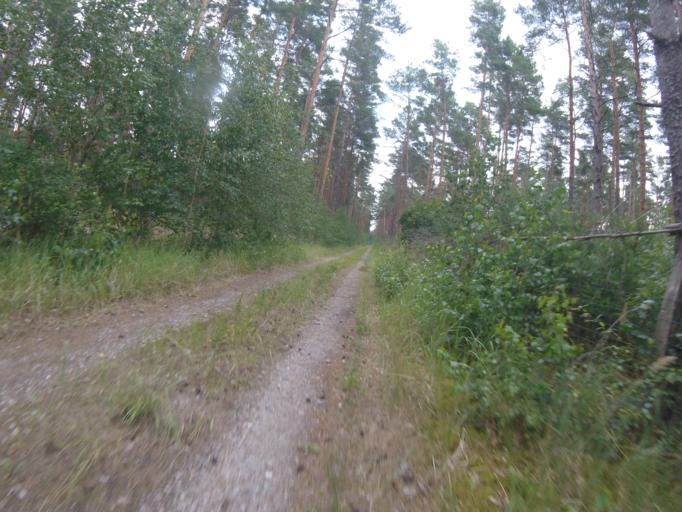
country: DE
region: Brandenburg
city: Schwerin
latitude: 52.1844
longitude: 13.6092
